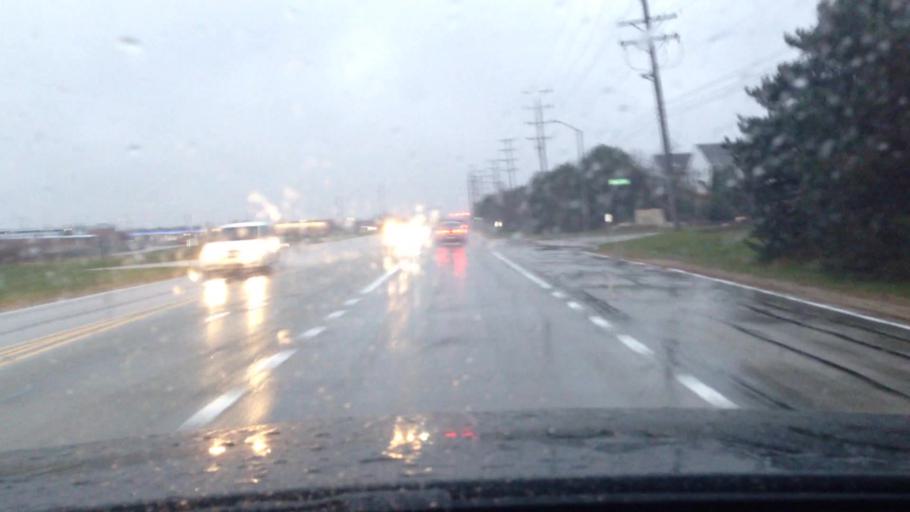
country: US
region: Illinois
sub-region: McHenry County
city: Huntley
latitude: 42.1801
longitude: -88.3838
